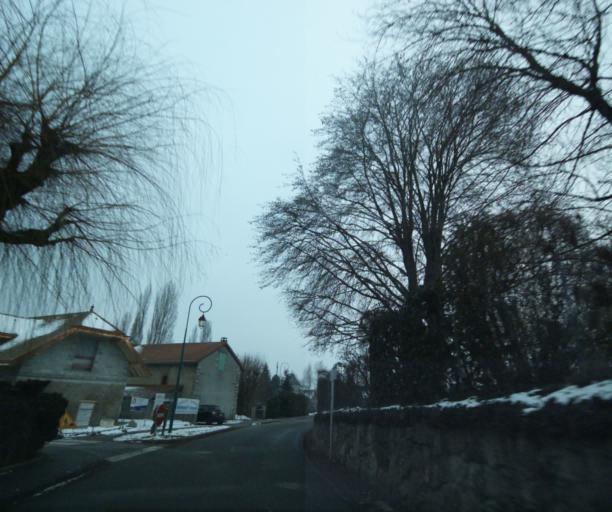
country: FR
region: Rhone-Alpes
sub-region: Departement de la Haute-Savoie
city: Reignier-Esery
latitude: 46.1440
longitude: 6.2375
